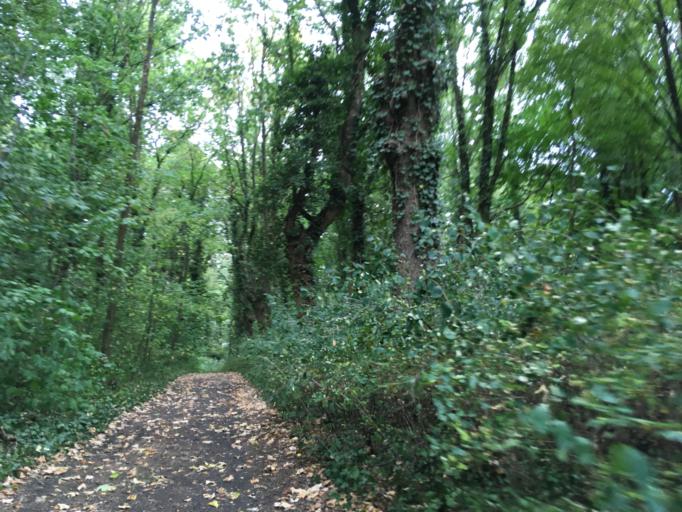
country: DE
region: Berlin
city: Niederschonhausen
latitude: 52.5960
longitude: 13.4105
